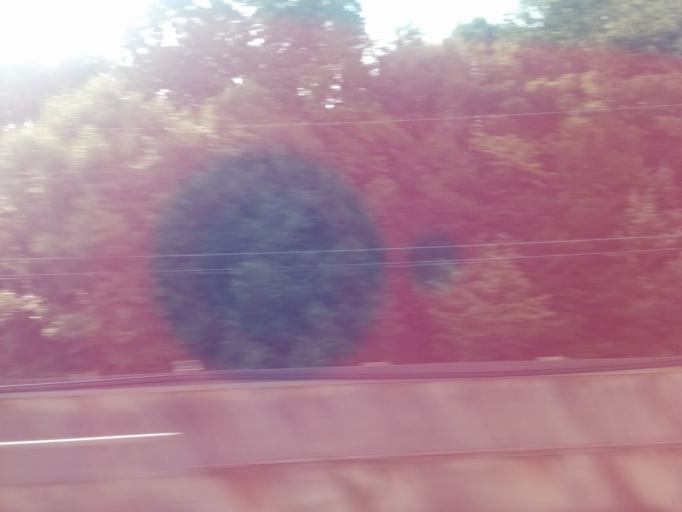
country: JP
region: Shiga Prefecture
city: Moriyama
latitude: 35.0749
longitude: 136.0399
